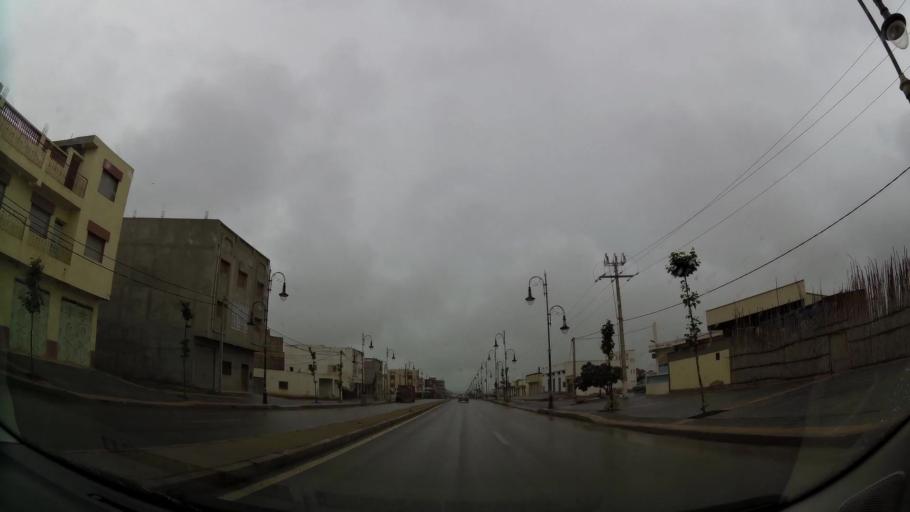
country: MA
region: Taza-Al Hoceima-Taounate
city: Imzourene
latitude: 35.1636
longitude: -3.8558
